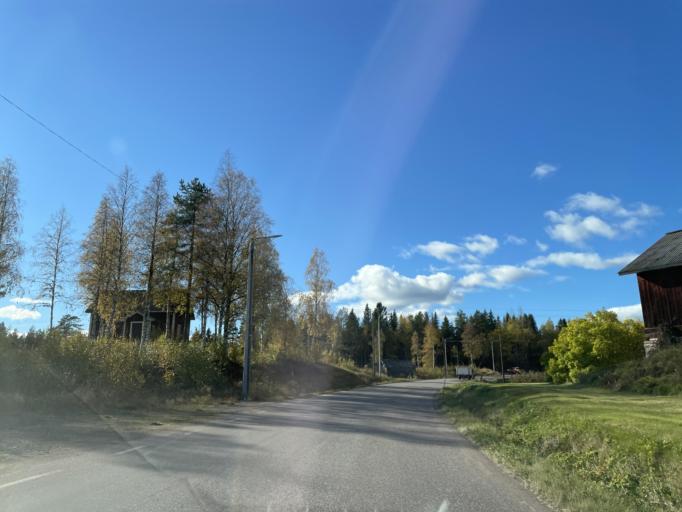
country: SE
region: Dalarna
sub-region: Malung-Saelens kommun
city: Malung
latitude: 60.9033
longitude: 13.3756
